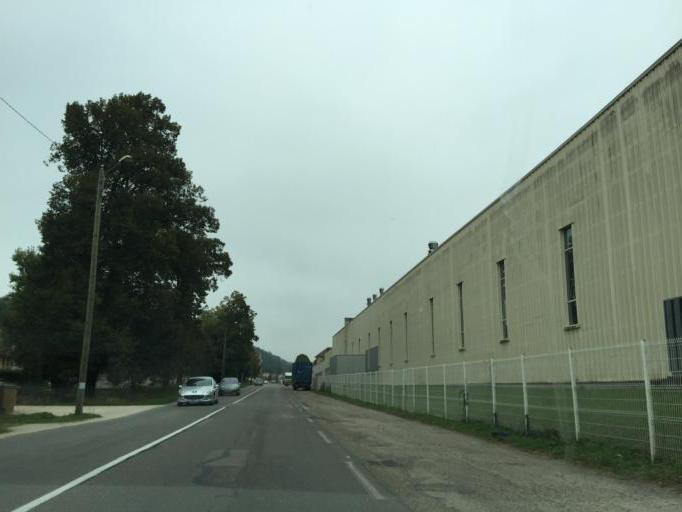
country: FR
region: Rhone-Alpes
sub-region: Departement de l'Isere
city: Saint-Clair-de-la-Tour
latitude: 45.5728
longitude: 5.4734
